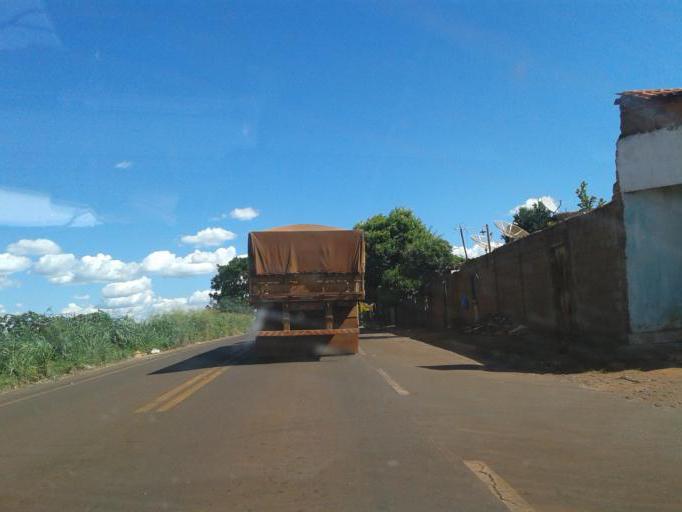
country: BR
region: Minas Gerais
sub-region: Capinopolis
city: Capinopolis
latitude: -18.6852
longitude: -49.5636
